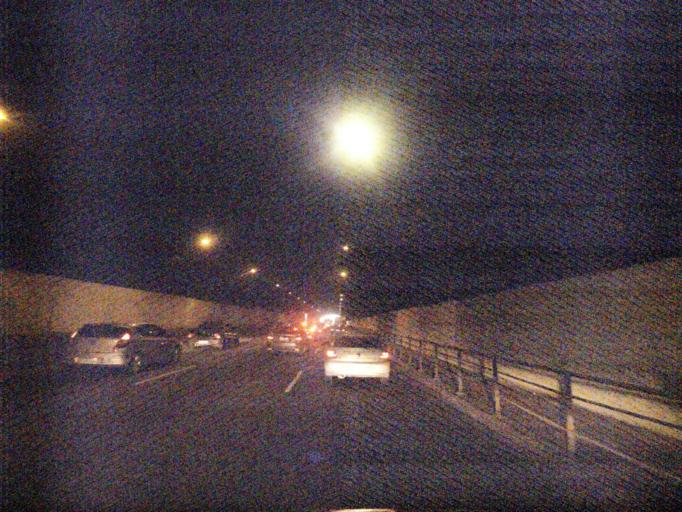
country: BR
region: Rio de Janeiro
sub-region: Niteroi
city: Niteroi
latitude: -22.9114
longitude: -43.0987
